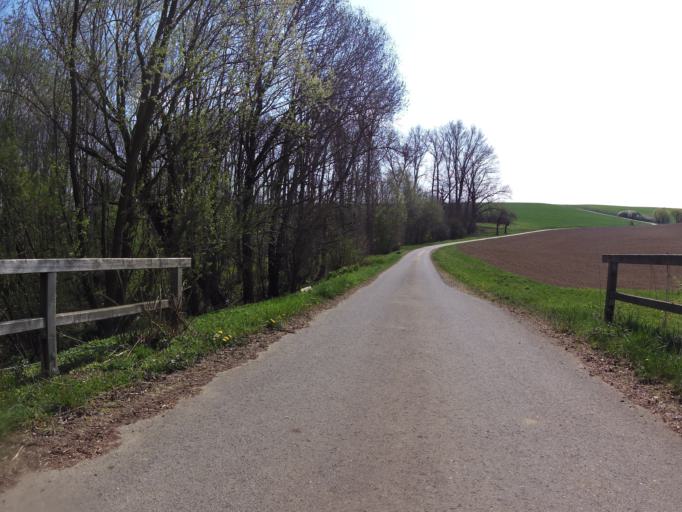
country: DE
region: Bavaria
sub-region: Regierungsbezirk Unterfranken
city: Dettelbach
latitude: 49.8215
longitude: 10.1370
